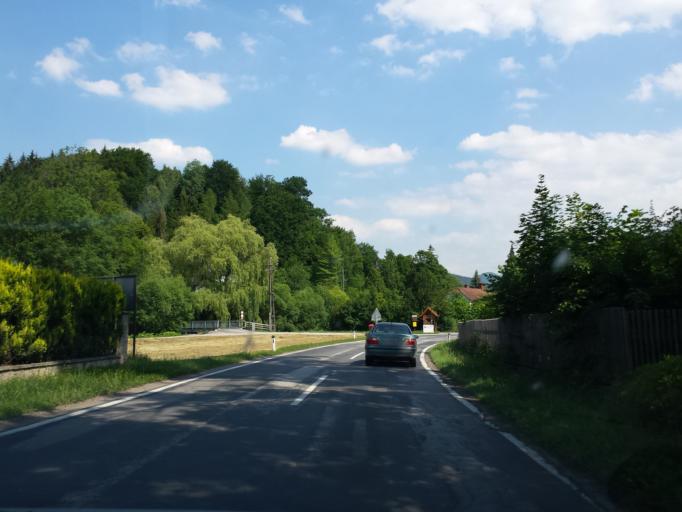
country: AT
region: Lower Austria
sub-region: Politischer Bezirk Lilienfeld
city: Ramsau
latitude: 48.0090
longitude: 15.7907
